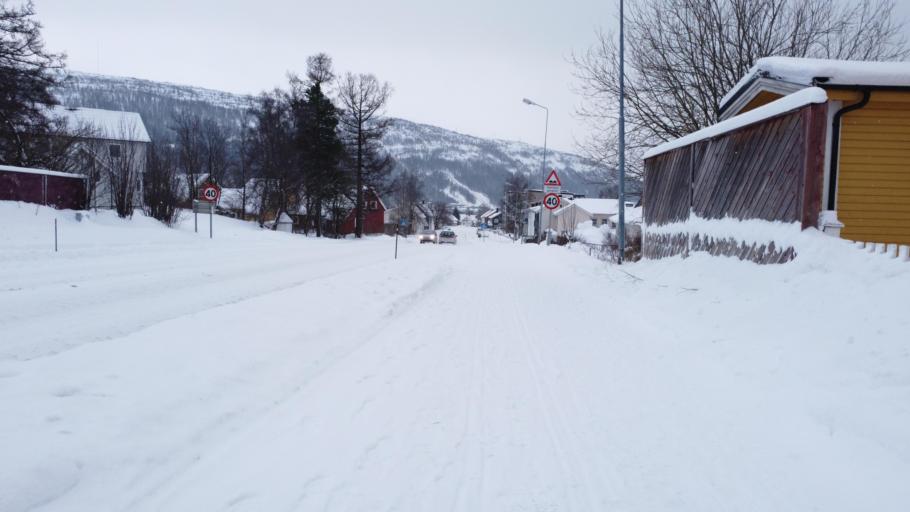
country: NO
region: Nordland
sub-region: Rana
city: Mo i Rana
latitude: 66.3156
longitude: 14.1558
